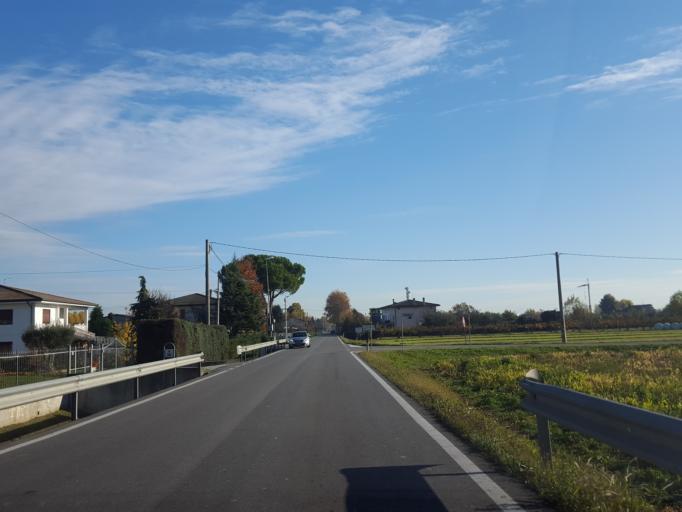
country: IT
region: Veneto
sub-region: Provincia di Padova
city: Piazzola sul Brenta
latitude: 45.5387
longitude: 11.7647
